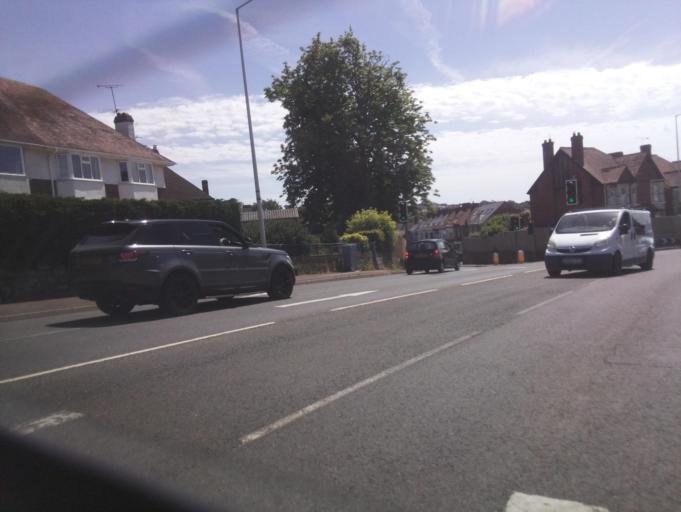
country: GB
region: England
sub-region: Devon
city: Exmouth
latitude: 50.6287
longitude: -3.4088
